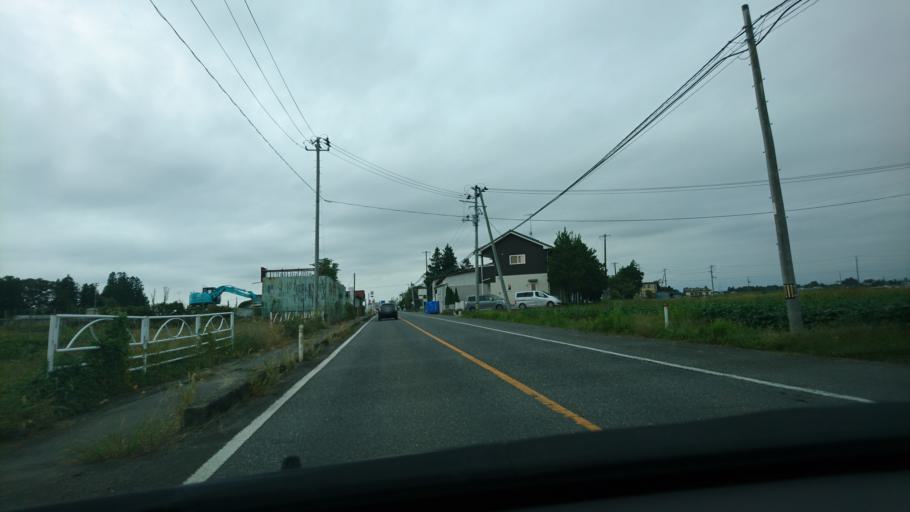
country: JP
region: Iwate
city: Ichinoseki
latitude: 38.7587
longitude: 141.0751
